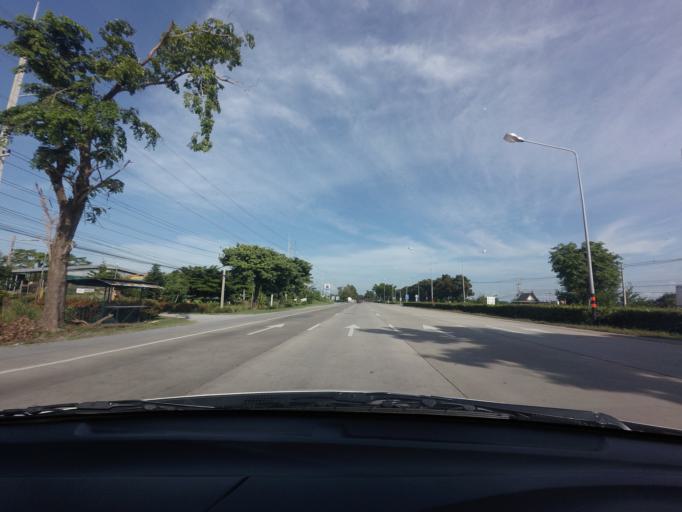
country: TH
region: Suphan Buri
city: Bang Pla Ma
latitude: 14.4292
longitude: 100.1449
